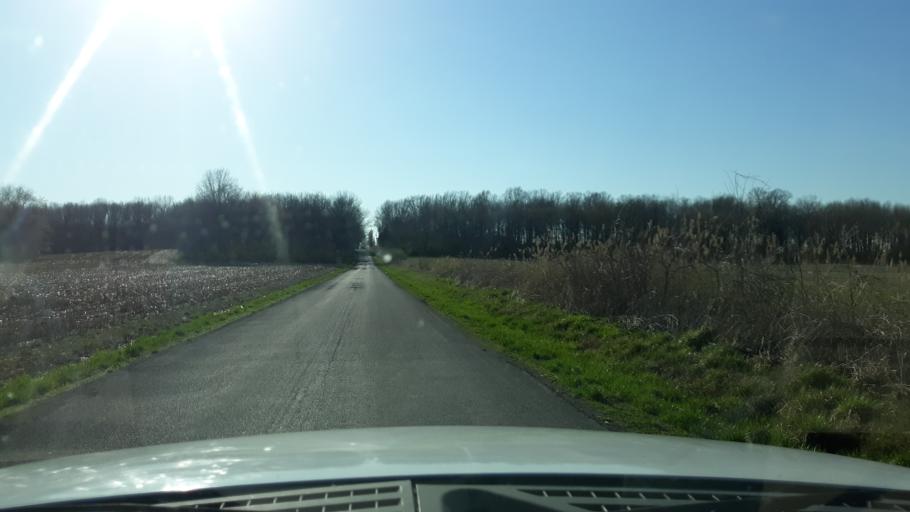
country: US
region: Illinois
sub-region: Saline County
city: Harrisburg
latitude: 37.7628
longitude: -88.5730
